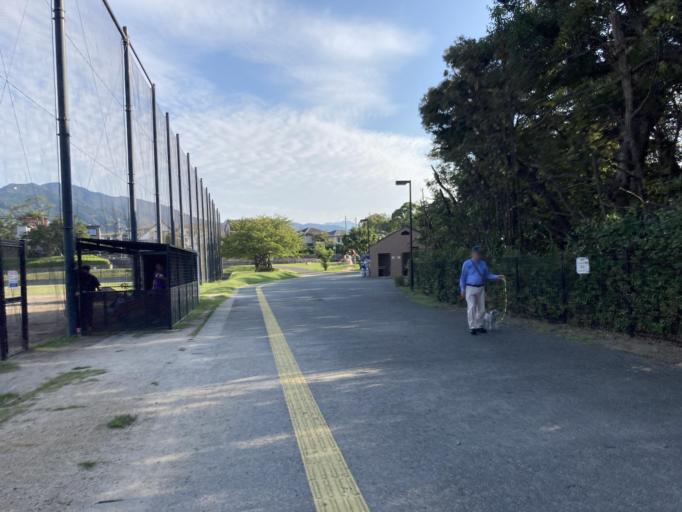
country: JP
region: Fukuoka
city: Fukuoka-shi
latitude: 33.5509
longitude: 130.3552
